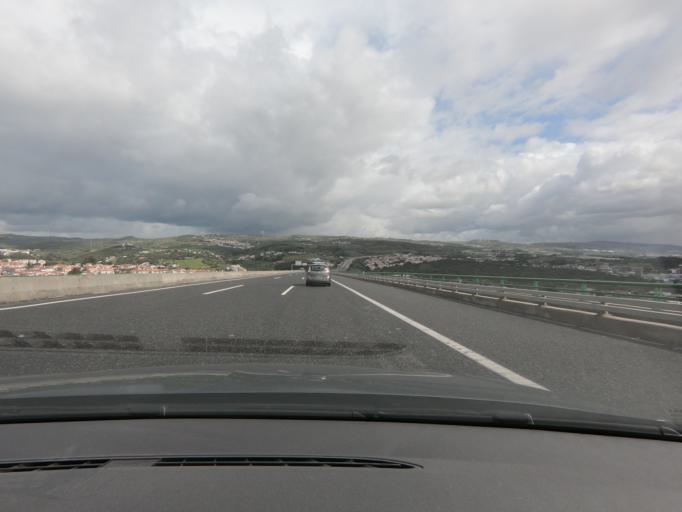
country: PT
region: Lisbon
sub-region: Loures
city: Loures
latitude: 38.8341
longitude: -9.1895
